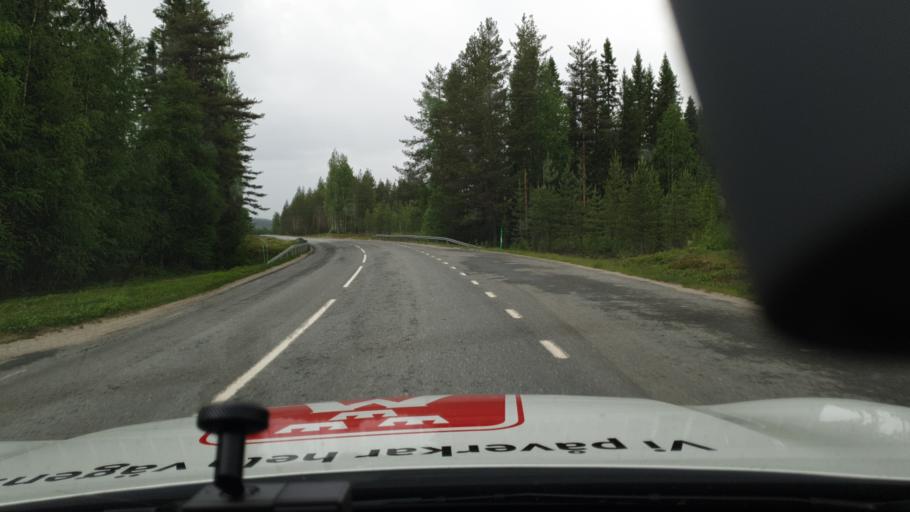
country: SE
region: Vaesterbotten
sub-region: Lycksele Kommun
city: Lycksele
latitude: 64.4324
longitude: 18.9739
